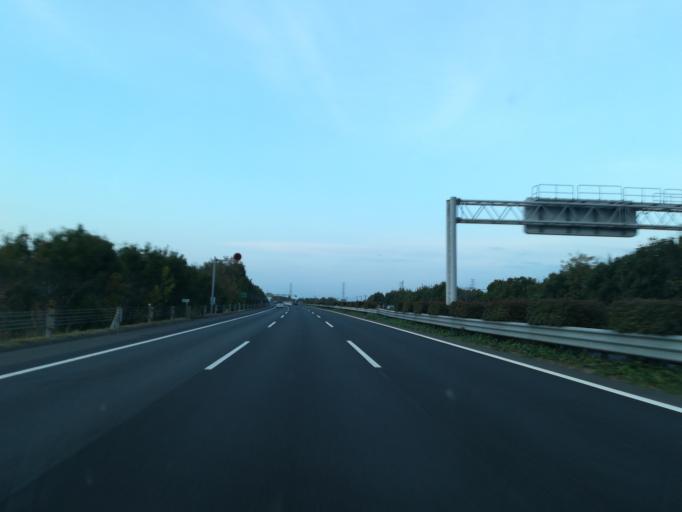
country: JP
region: Gunma
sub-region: Sawa-gun
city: Tamamura
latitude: 36.2959
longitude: 139.0970
